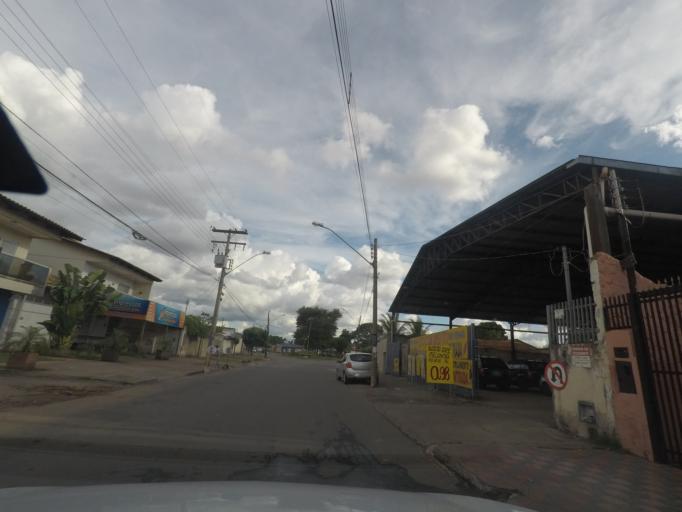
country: BR
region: Goias
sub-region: Goiania
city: Goiania
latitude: -16.7122
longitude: -49.3038
